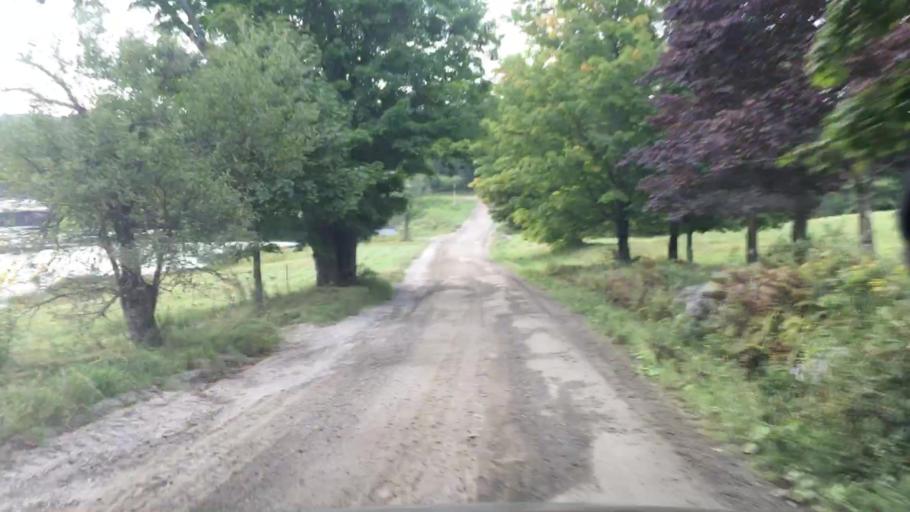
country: US
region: Vermont
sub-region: Windham County
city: Dover
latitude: 42.8324
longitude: -72.8005
